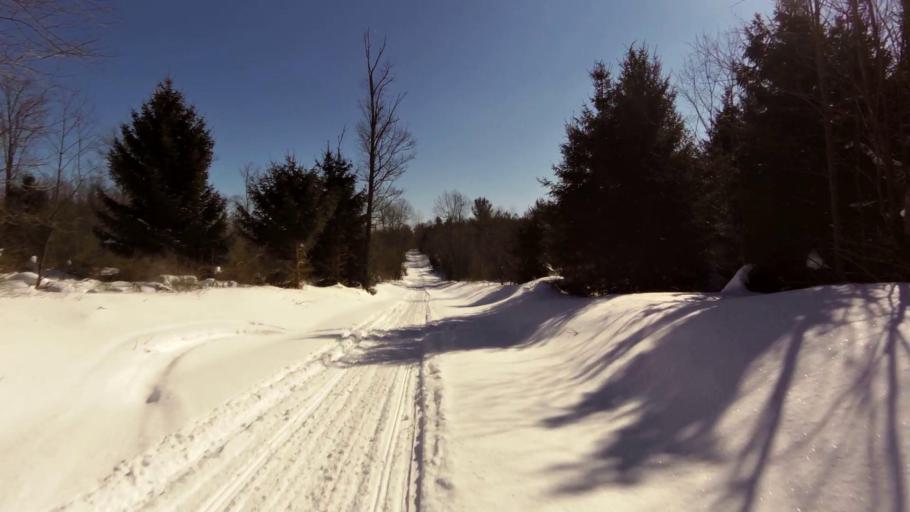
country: US
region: New York
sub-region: Cattaraugus County
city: Franklinville
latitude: 42.3429
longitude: -78.3637
